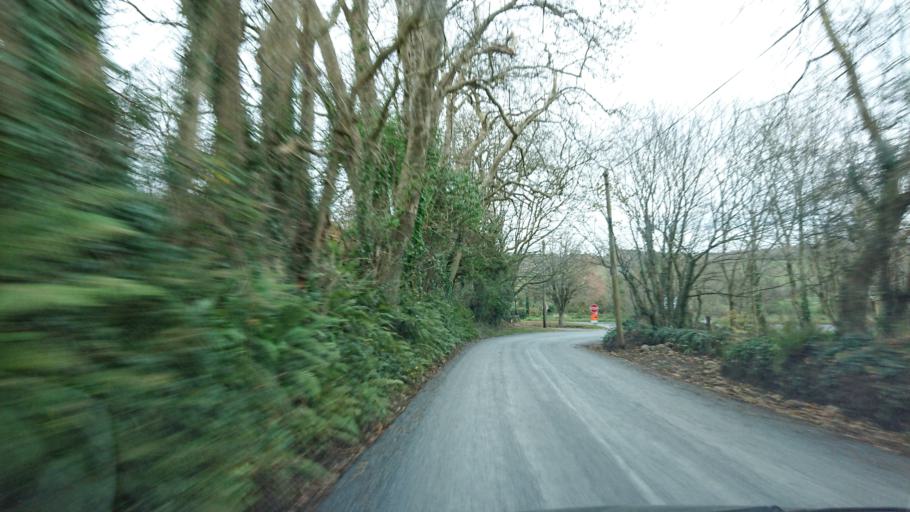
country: IE
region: Munster
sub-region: Waterford
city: Dunmore East
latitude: 52.2017
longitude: -7.0257
